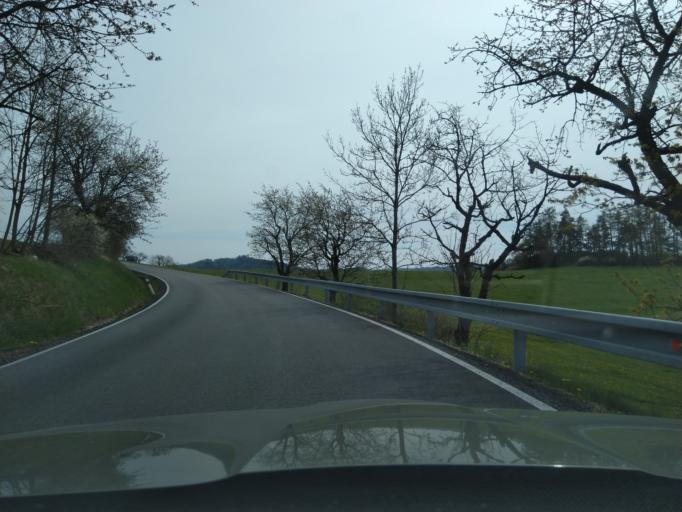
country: CZ
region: Jihocesky
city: Ckyne
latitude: 49.1157
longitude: 13.8153
